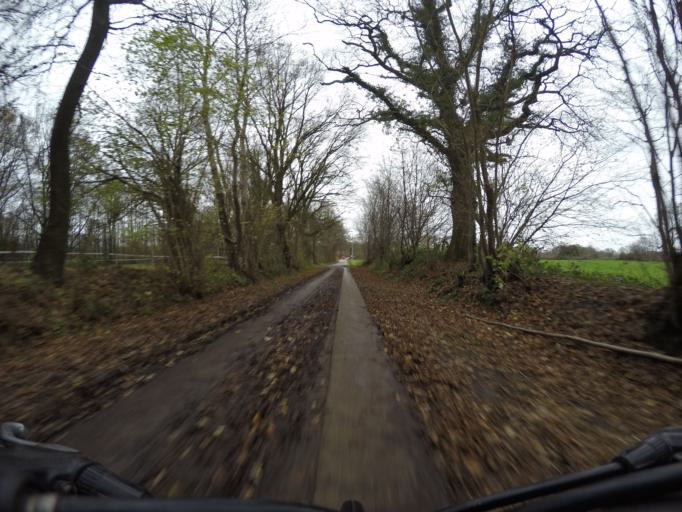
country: DE
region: Schleswig-Holstein
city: Quickborn
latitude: 53.7209
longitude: 9.8950
